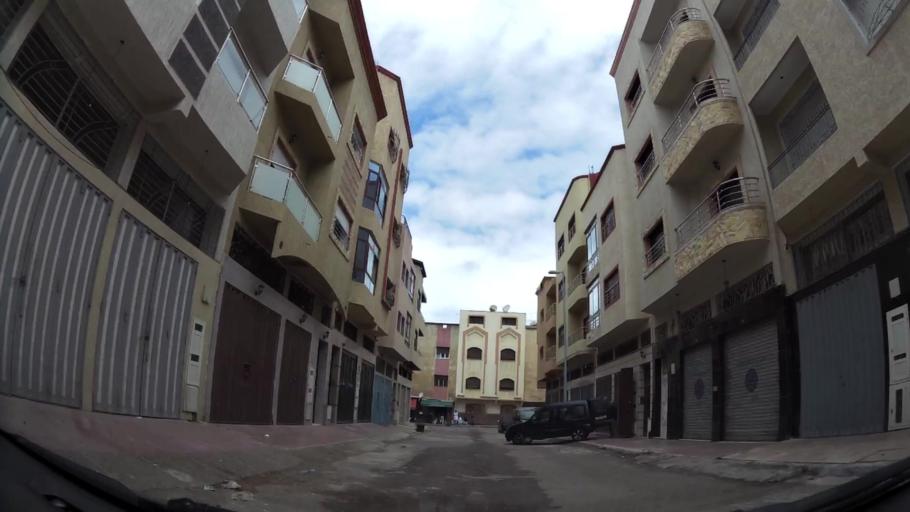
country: MA
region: Grand Casablanca
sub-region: Casablanca
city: Casablanca
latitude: 33.5356
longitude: -7.5983
